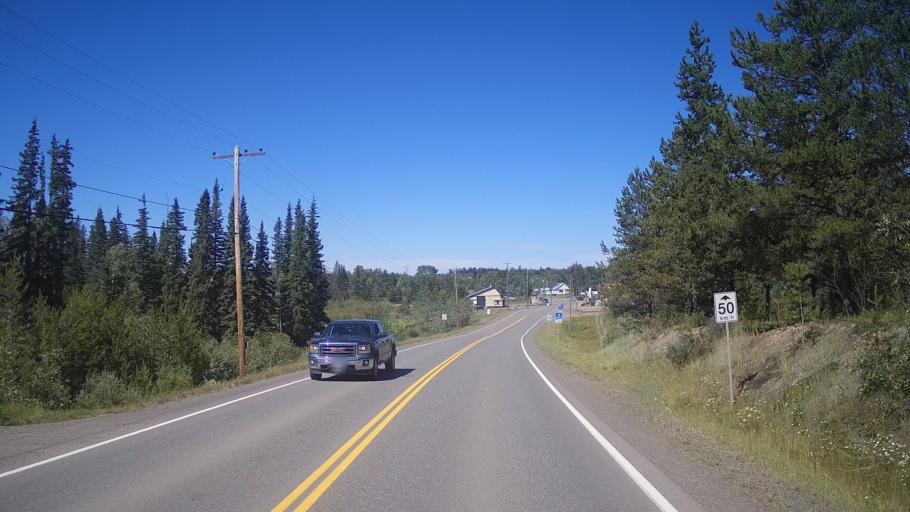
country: CA
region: British Columbia
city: Cache Creek
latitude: 51.5547
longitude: -121.2007
